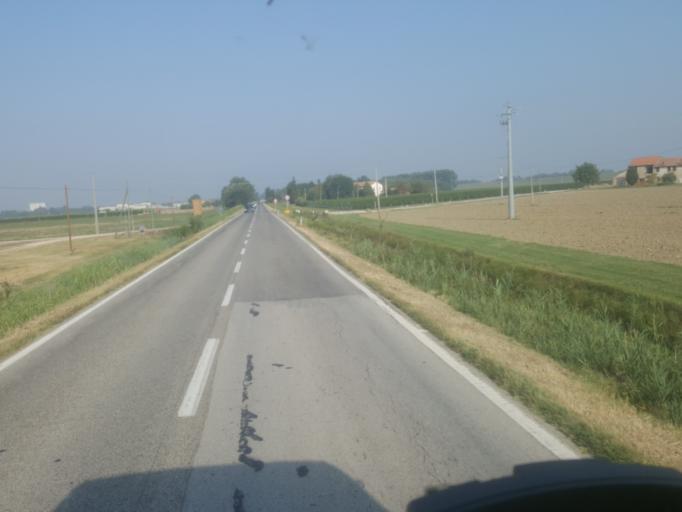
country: IT
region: Emilia-Romagna
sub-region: Provincia di Ravenna
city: Lavezzola
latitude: 44.5644
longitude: 11.9018
